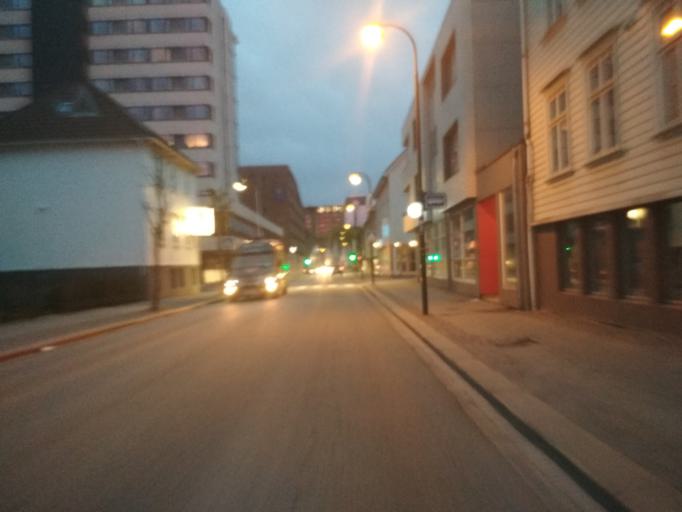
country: NO
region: Rogaland
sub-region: Stavanger
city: Stavanger
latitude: 58.9701
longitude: 5.7255
